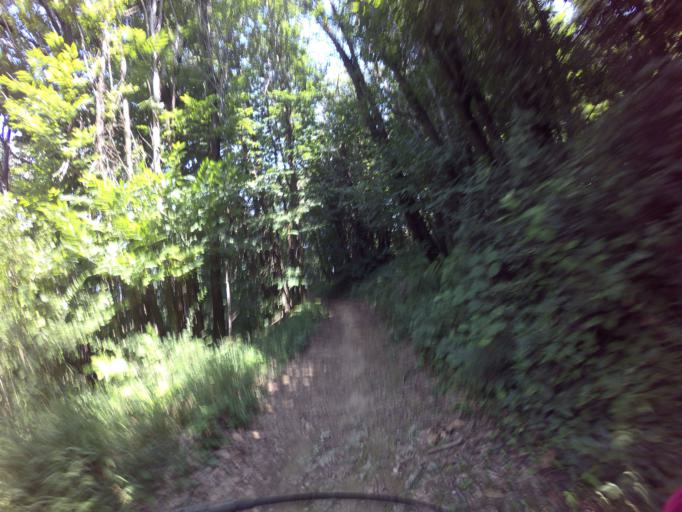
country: IT
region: Piedmont
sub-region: Provincia di Cuneo
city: Roccaforte Mondovi
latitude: 44.3338
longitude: 7.7113
